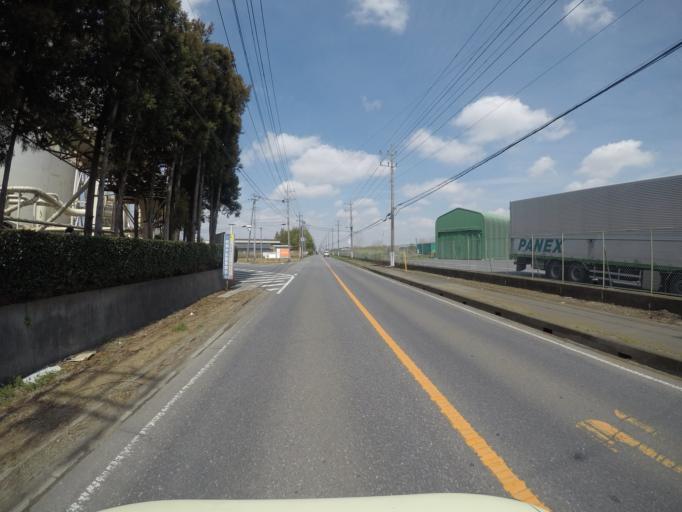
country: JP
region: Ibaraki
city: Tsukuba
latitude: 36.2308
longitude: 140.0584
